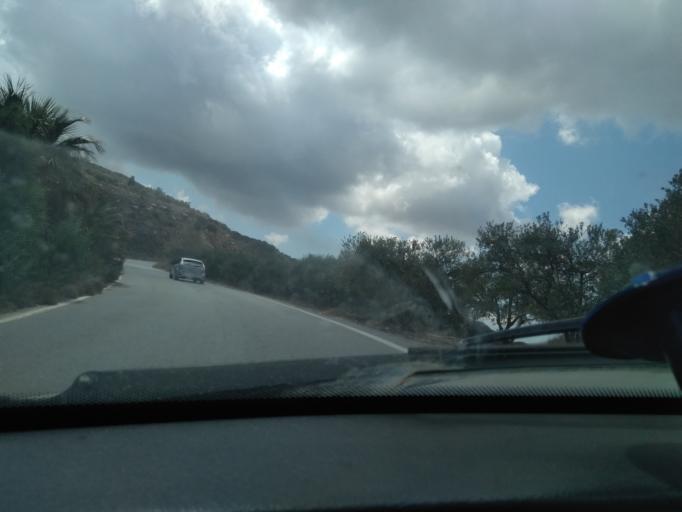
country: GR
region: Crete
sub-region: Nomos Lasithiou
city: Siteia
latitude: 35.0973
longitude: 26.0713
